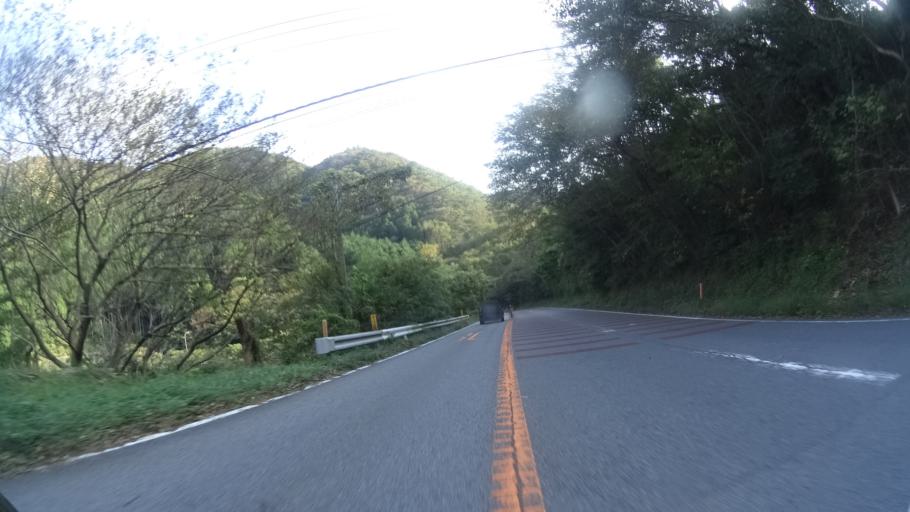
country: JP
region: Oita
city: Beppu
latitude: 33.2772
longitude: 131.4488
